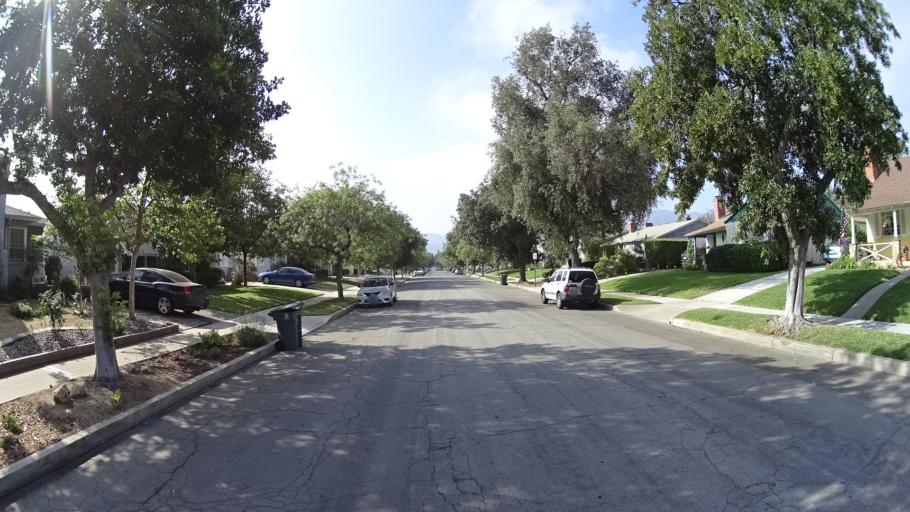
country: US
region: California
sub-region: Los Angeles County
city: Burbank
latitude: 34.1679
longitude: -118.3196
